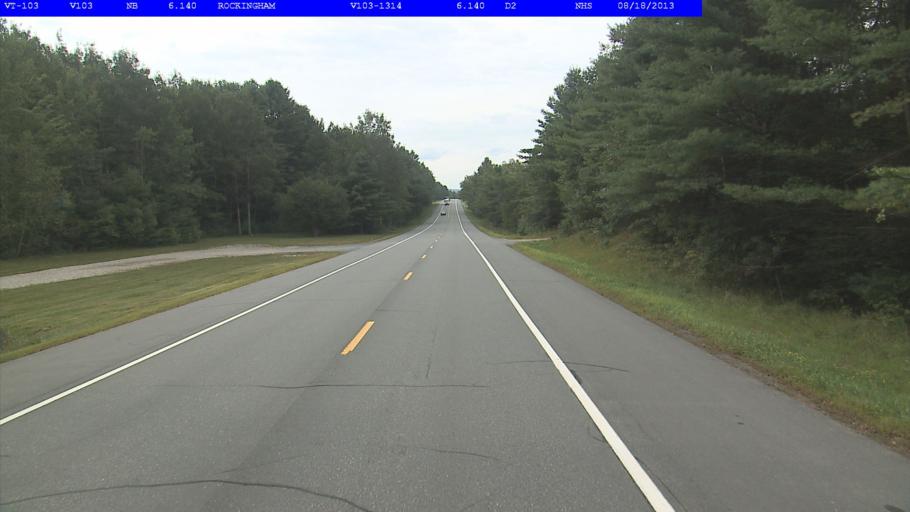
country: US
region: Vermont
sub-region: Windsor County
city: Chester
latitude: 43.2287
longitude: -72.5448
